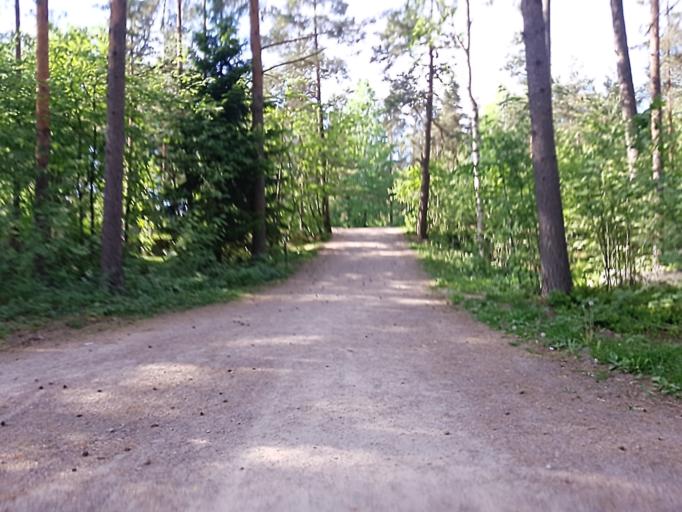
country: FI
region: Uusimaa
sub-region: Helsinki
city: Helsinki
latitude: 60.2356
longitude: 24.9591
